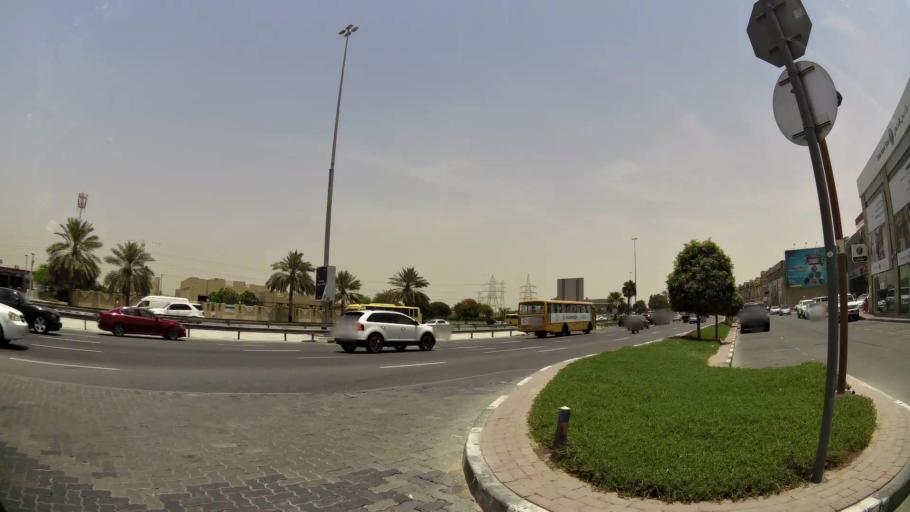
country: AE
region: Ash Shariqah
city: Sharjah
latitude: 25.2145
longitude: 55.3793
